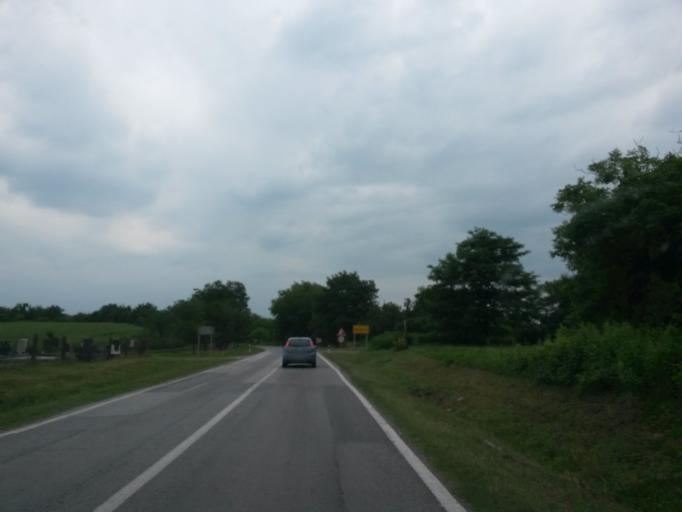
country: HR
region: Vukovarsko-Srijemska
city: Lovas
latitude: 45.2502
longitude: 19.2100
